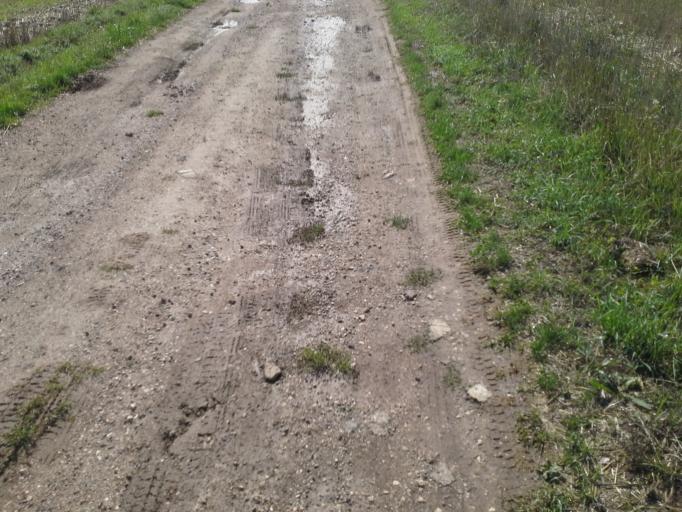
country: FR
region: Centre
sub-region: Departement du Loir-et-Cher
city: Villiers-sur-Loir
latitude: 47.8221
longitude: 0.9885
